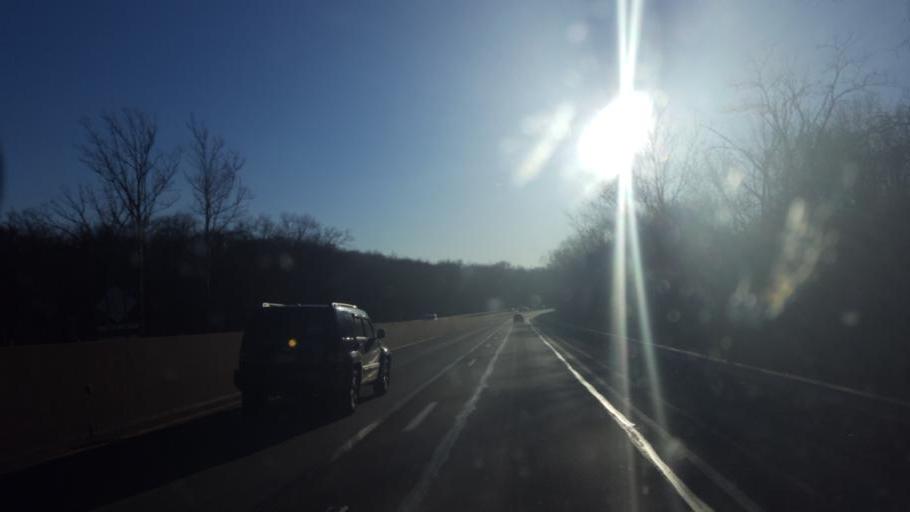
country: US
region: Pennsylvania
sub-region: Westmoreland County
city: New Stanton
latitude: 40.2120
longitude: -79.6507
